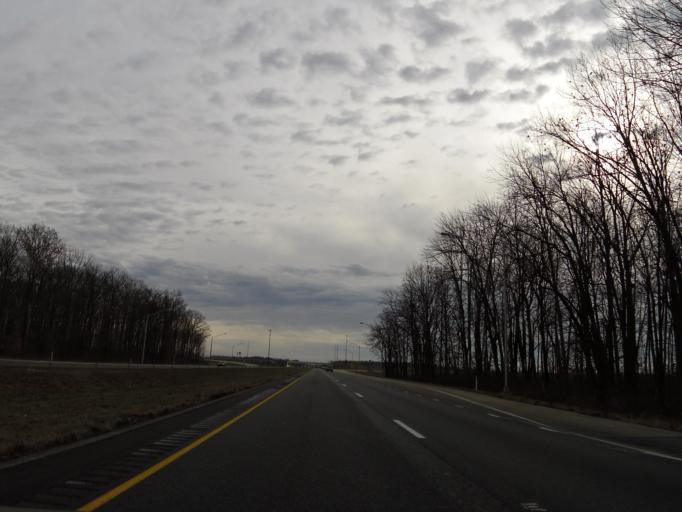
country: US
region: Indiana
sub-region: Hendricks County
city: Fairfield Heights
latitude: 39.8443
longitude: -86.3629
